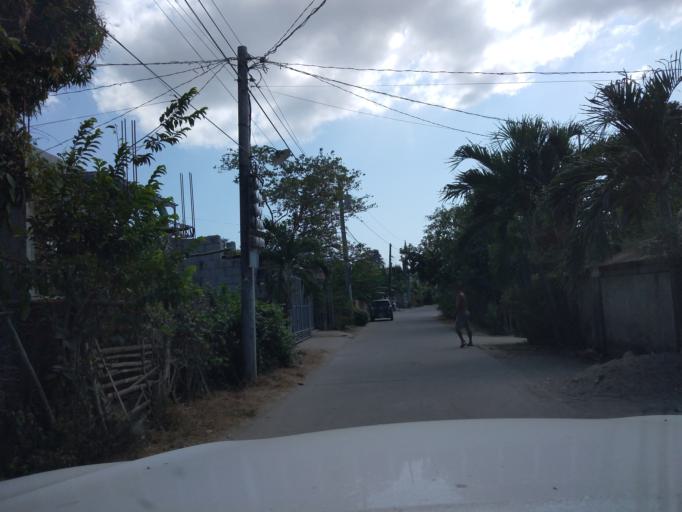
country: PH
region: Central Luzon
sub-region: Province of Pampanga
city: Candaba
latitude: 15.0889
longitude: 120.8146
